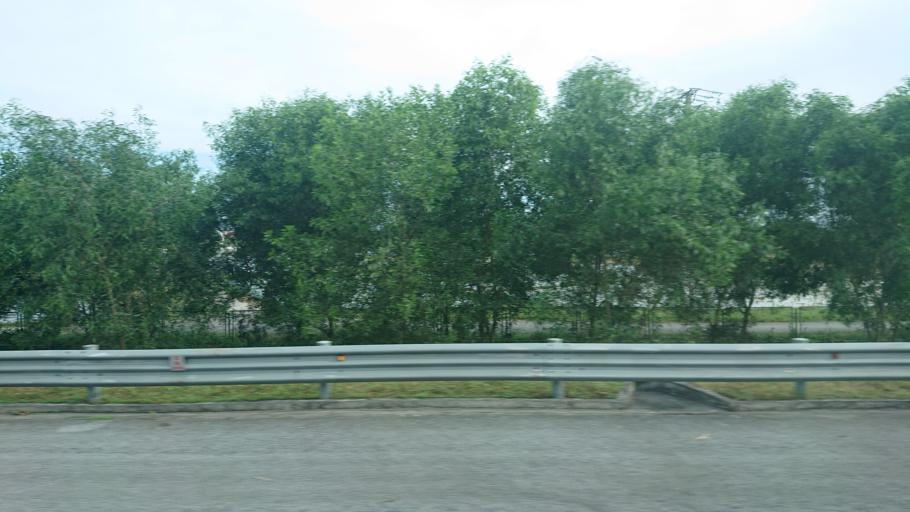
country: VN
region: Hai Phong
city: Nui Doi
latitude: 20.7658
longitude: 106.6496
